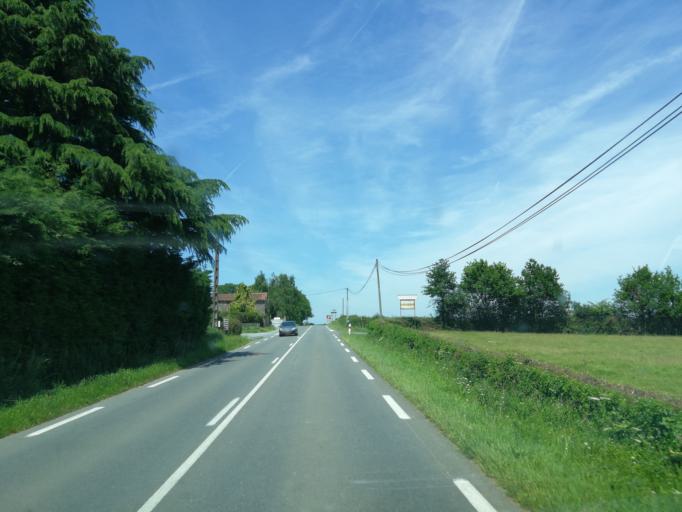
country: FR
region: Pays de la Loire
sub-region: Departement de la Vendee
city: Antigny
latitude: 46.5794
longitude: -0.7944
